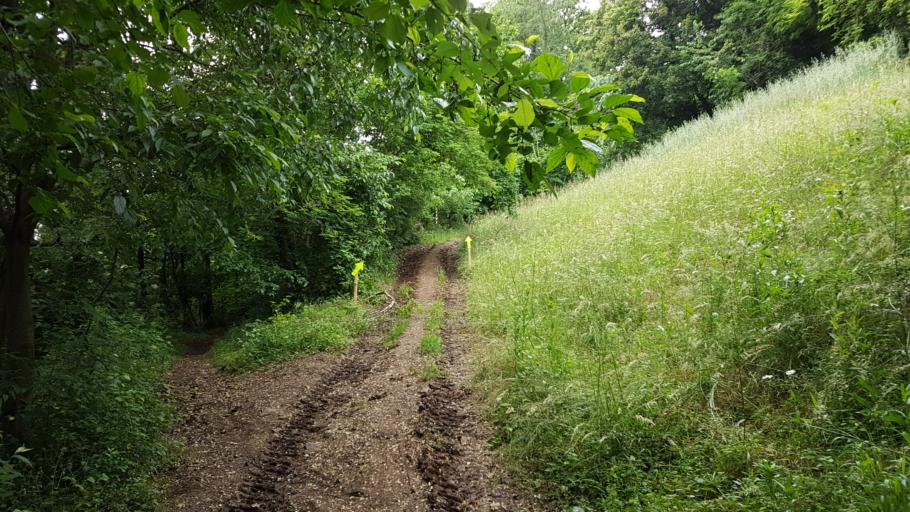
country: IT
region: Veneto
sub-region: Provincia di Vicenza
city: Arzignano
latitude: 45.5522
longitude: 11.3380
